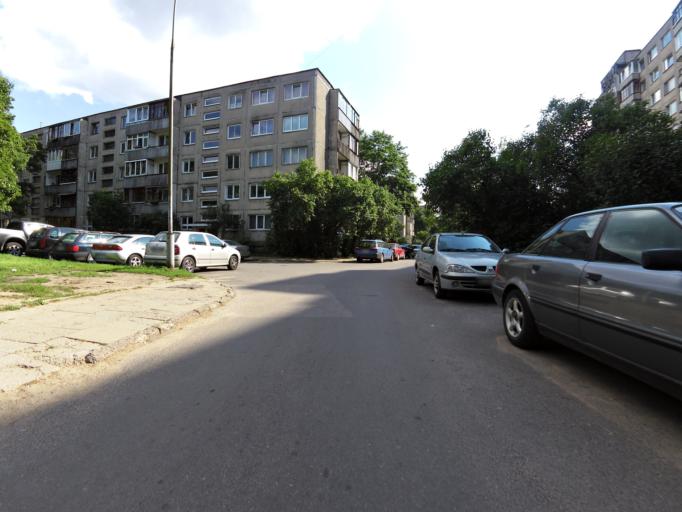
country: LT
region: Vilnius County
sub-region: Vilnius
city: Vilnius
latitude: 54.7039
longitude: 25.2958
